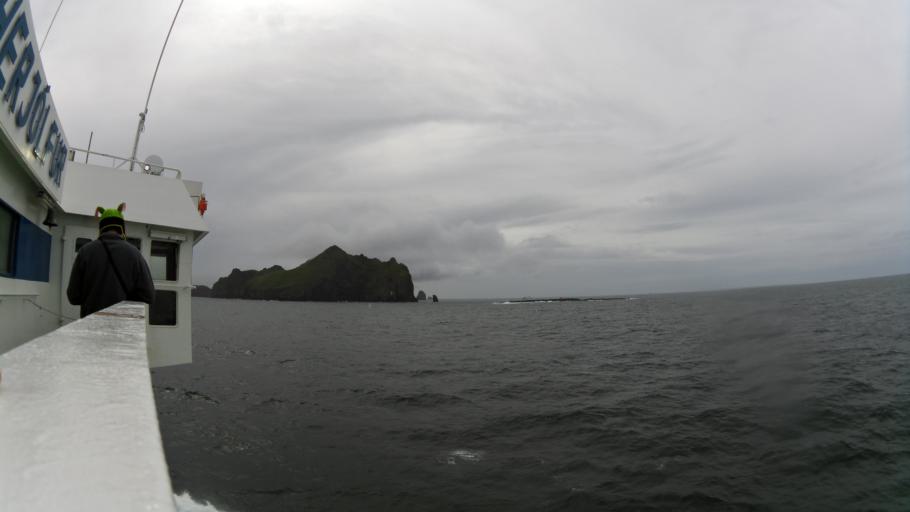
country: IS
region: South
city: Vestmannaeyjar
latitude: 63.4604
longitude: -20.2179
